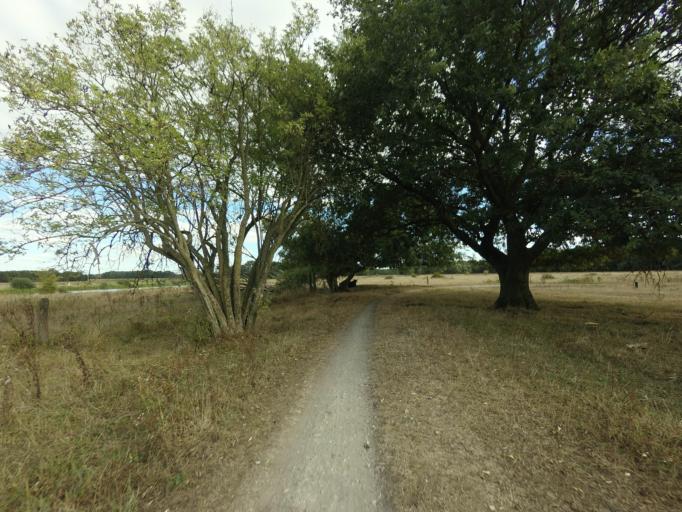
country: NL
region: North Brabant
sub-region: Gemeente Grave
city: Grave
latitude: 51.7247
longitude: 5.7479
